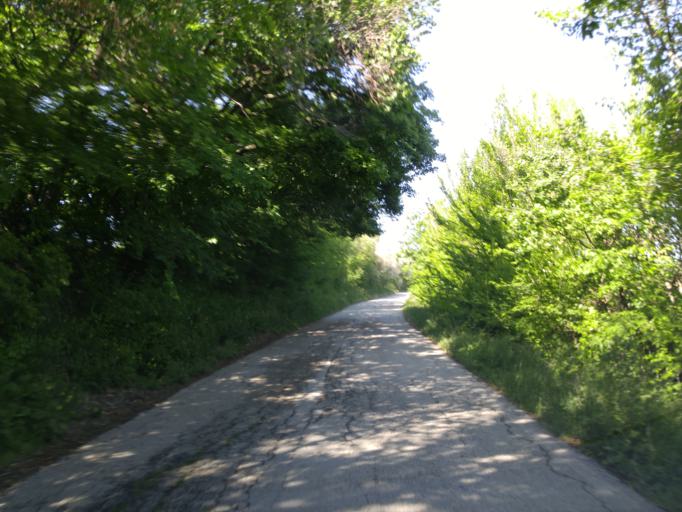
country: IT
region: The Marches
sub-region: Provincia di Pesaro e Urbino
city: Lucrezia
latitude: 43.7931
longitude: 12.9130
